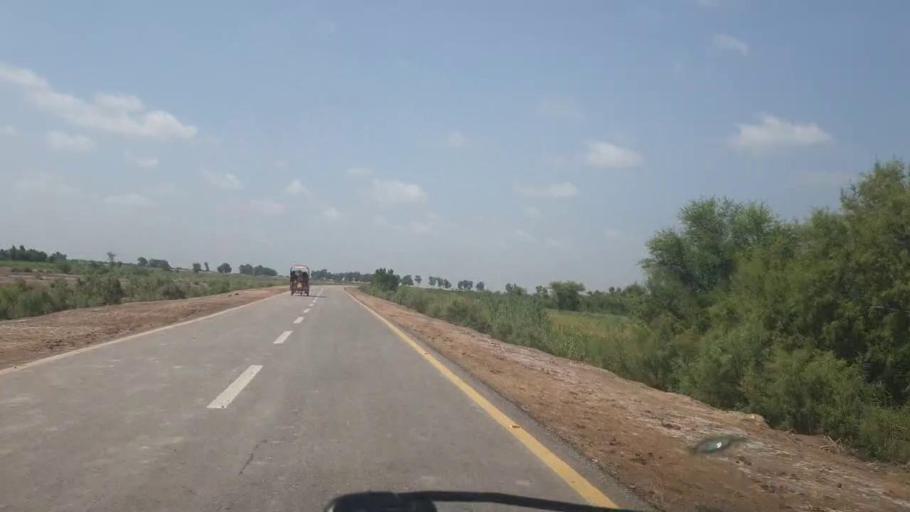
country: PK
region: Sindh
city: Berani
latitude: 25.7086
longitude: 68.9422
